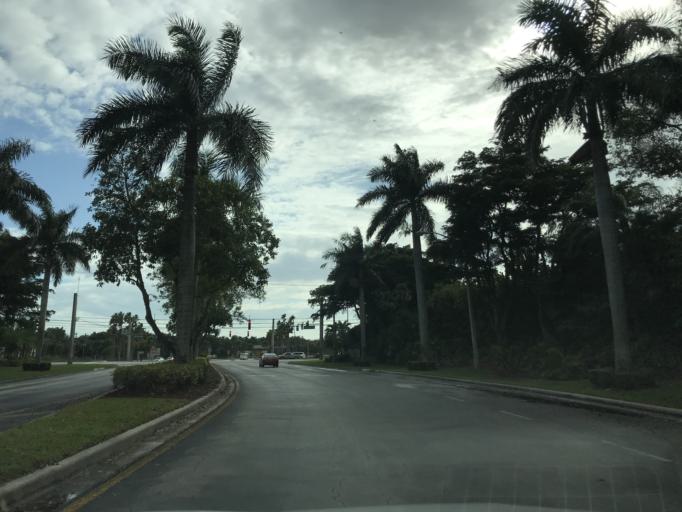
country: US
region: Florida
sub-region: Palm Beach County
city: Villages of Oriole
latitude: 26.5292
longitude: -80.1703
